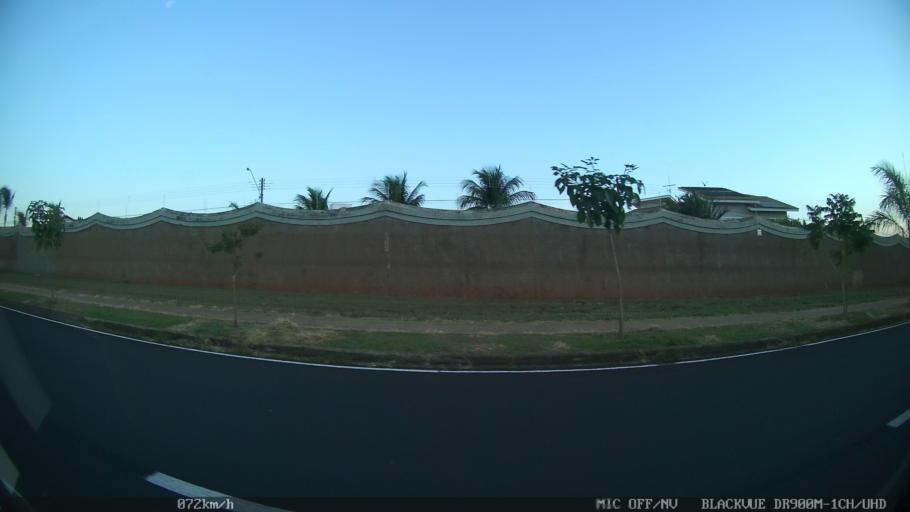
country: BR
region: Sao Paulo
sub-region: Sao Jose Do Rio Preto
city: Sao Jose do Rio Preto
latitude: -20.8168
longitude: -49.3430
